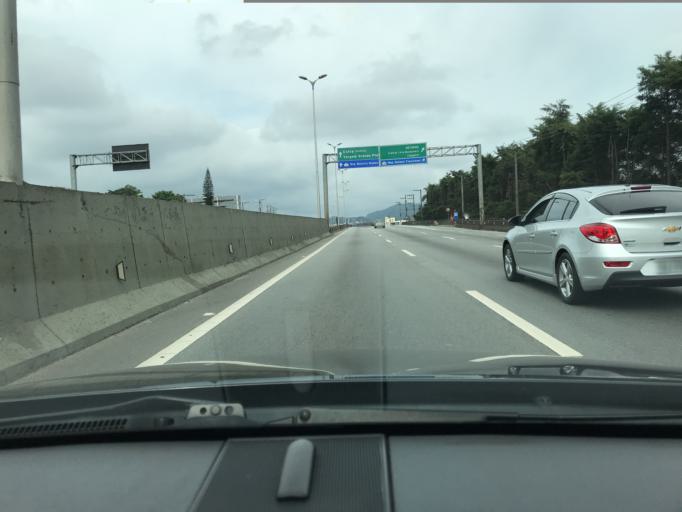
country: BR
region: Sao Paulo
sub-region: Cotia
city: Cotia
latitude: -23.6001
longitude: -46.9016
